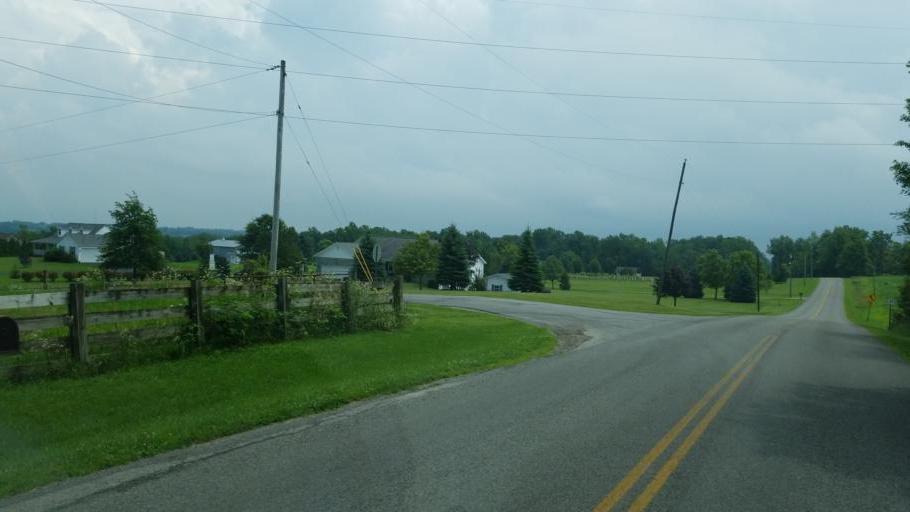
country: US
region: Ohio
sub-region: Logan County
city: Northwood
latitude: 40.4135
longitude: -83.7010
